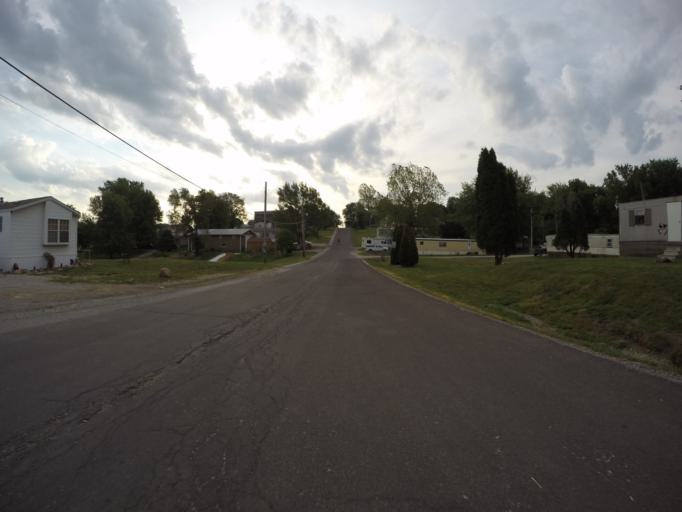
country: US
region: Kansas
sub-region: Doniphan County
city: Troy
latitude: 39.7847
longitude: -95.0944
